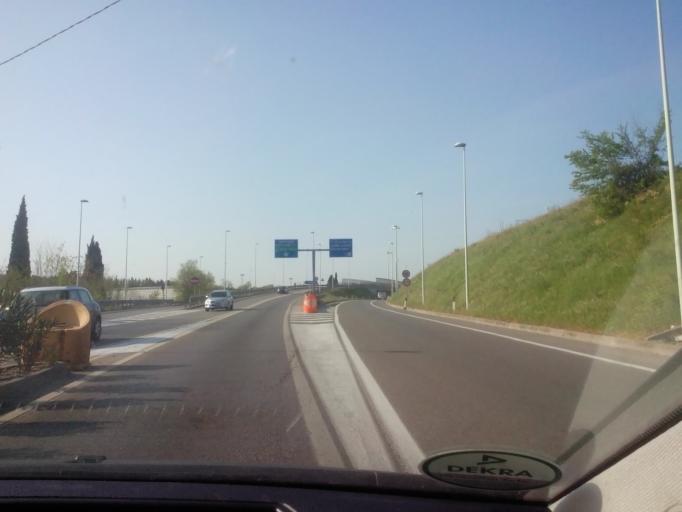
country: IT
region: Lombardy
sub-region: Provincia di Brescia
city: Desenzano del Garda
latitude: 45.4600
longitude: 10.5248
